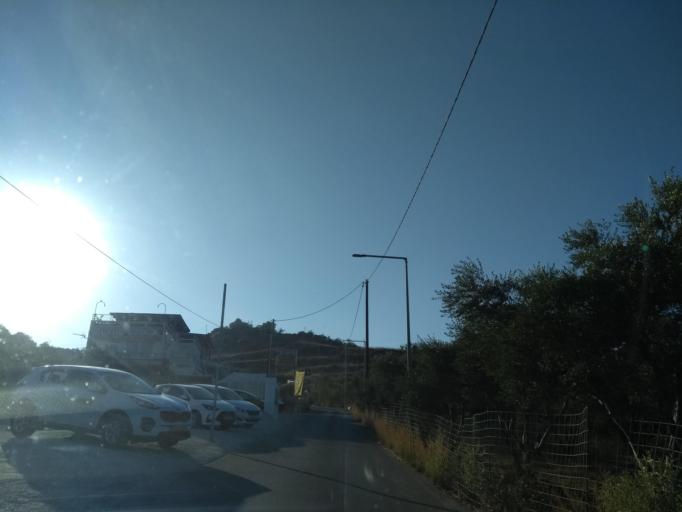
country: GR
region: Crete
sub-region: Nomos Chanias
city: Kalivai
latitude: 35.4659
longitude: 24.1551
